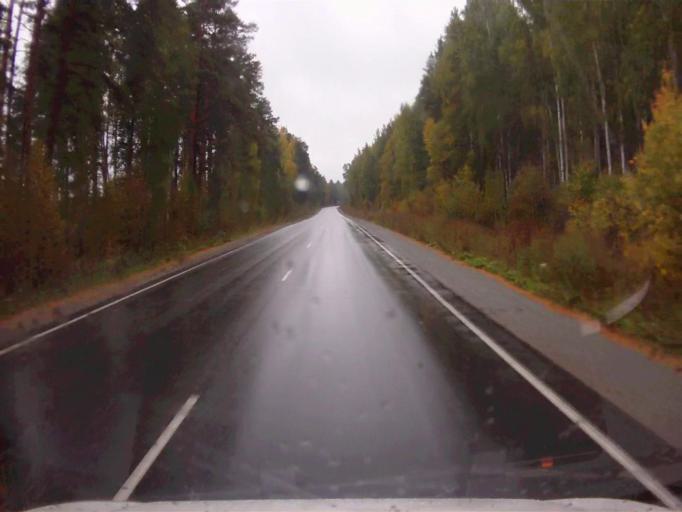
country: RU
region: Chelyabinsk
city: Kyshtym
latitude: 55.6387
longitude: 60.5930
